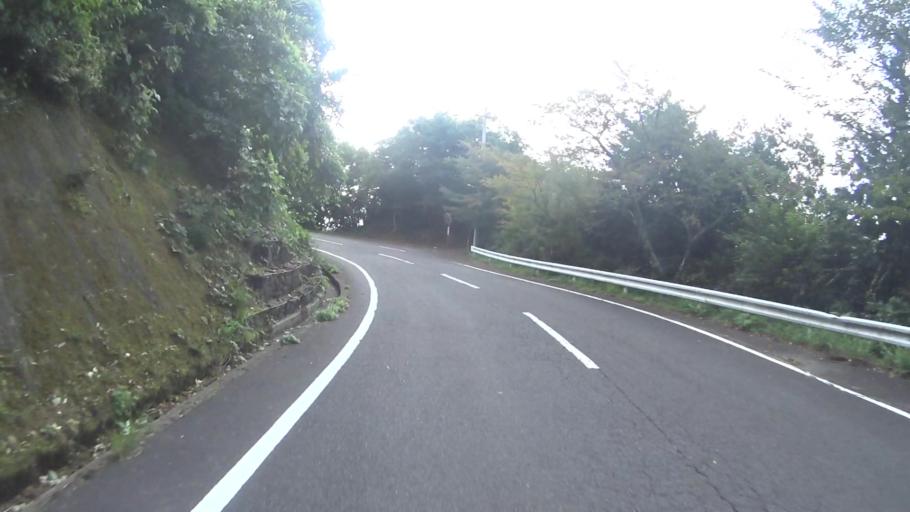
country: JP
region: Kyoto
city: Miyazu
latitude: 35.7419
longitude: 135.1734
